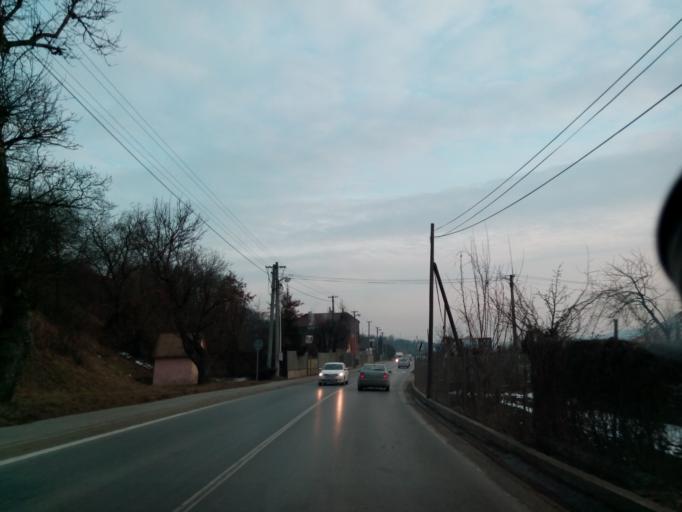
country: SK
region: Presovsky
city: Sabinov
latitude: 49.0881
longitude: 21.1152
